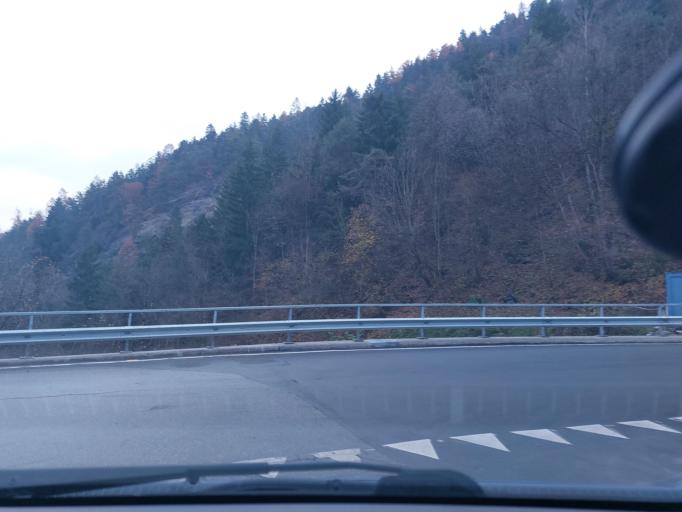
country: CH
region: Valais
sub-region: Conthey District
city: Chamoson
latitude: 46.2076
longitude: 7.2084
